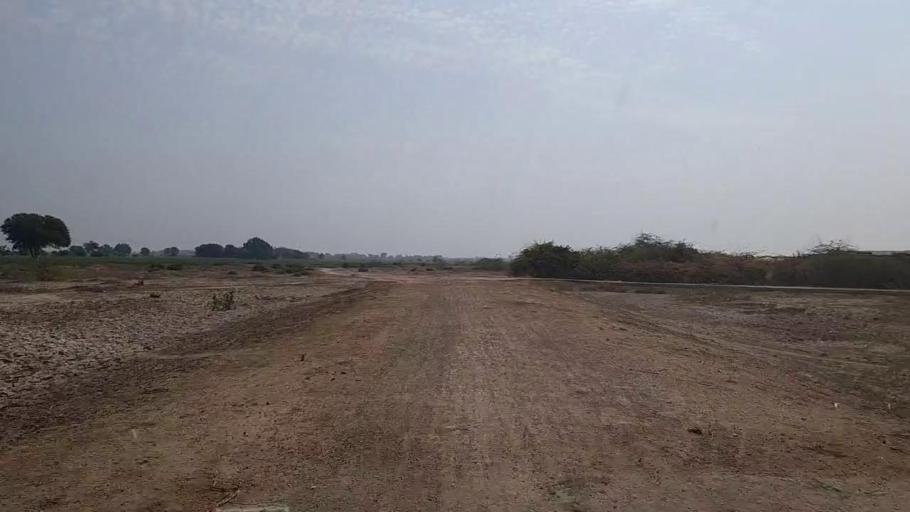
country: PK
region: Sindh
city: Mirwah Gorchani
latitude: 25.3422
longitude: 69.0789
